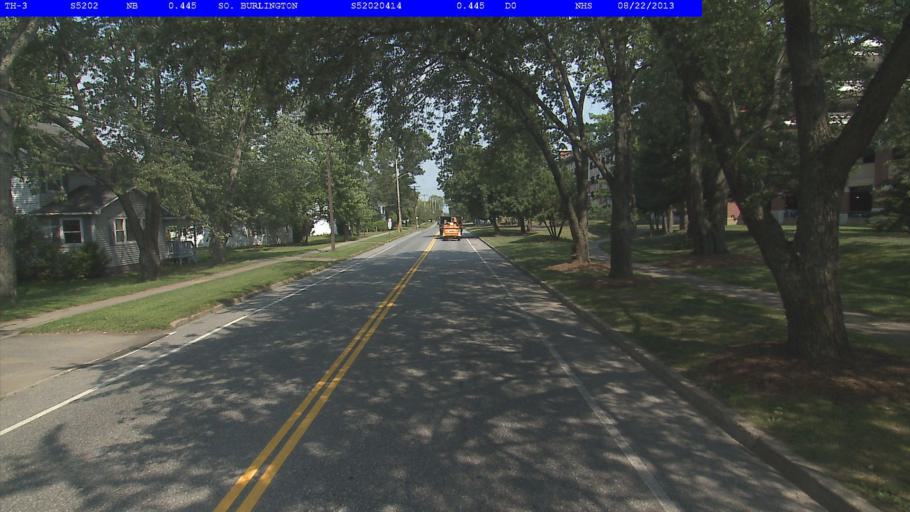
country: US
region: Vermont
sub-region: Chittenden County
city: South Burlington
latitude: 44.4692
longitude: -73.1568
